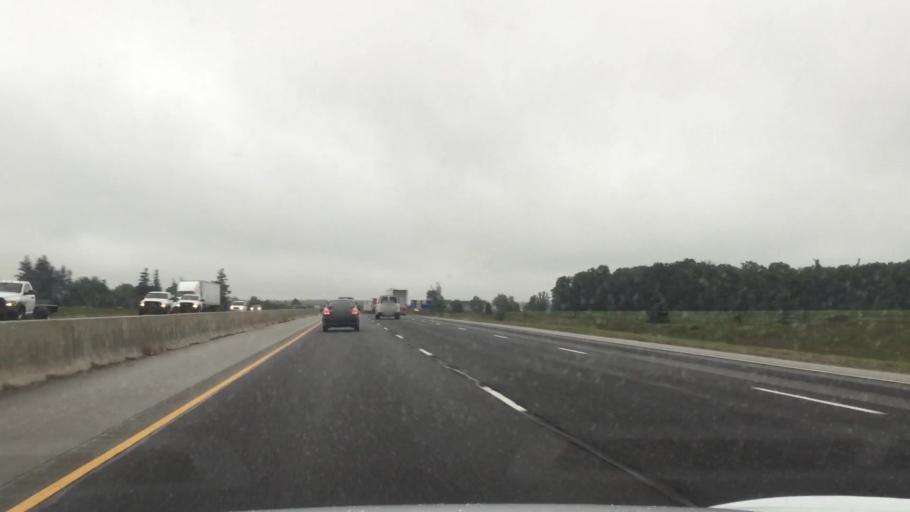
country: CA
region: Ontario
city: Kitchener
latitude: 43.3070
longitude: -80.4789
